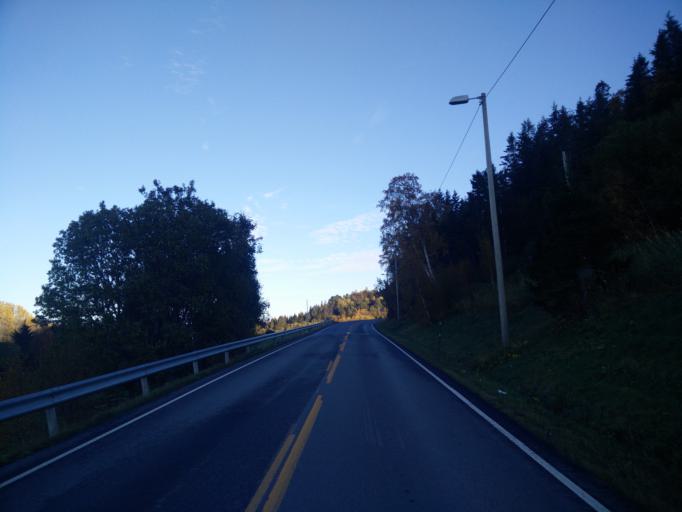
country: NO
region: Sor-Trondelag
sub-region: Skaun
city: Borsa
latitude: 63.3467
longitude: 10.0325
